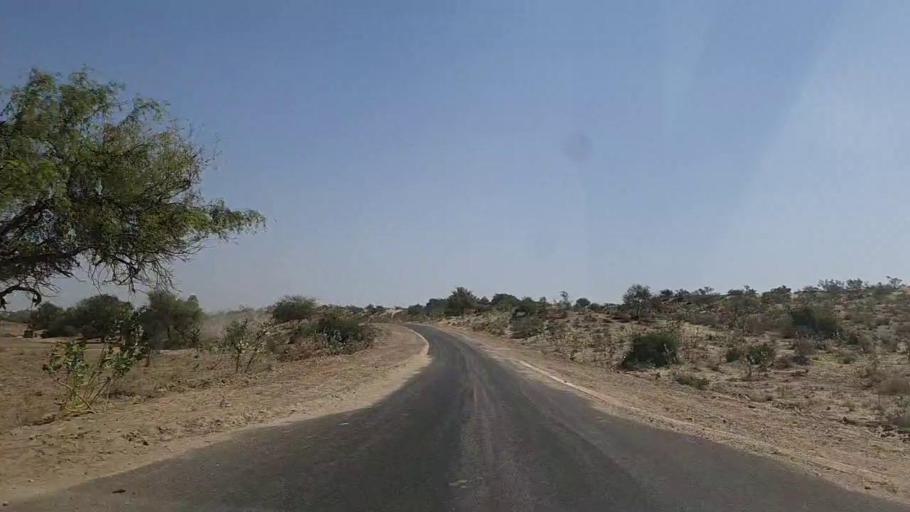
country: PK
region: Sindh
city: Diplo
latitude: 24.4809
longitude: 69.4845
